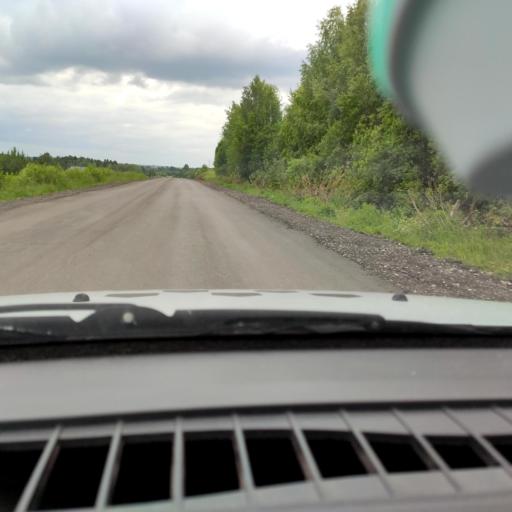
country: RU
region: Perm
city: Uinskoye
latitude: 57.1730
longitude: 56.5622
